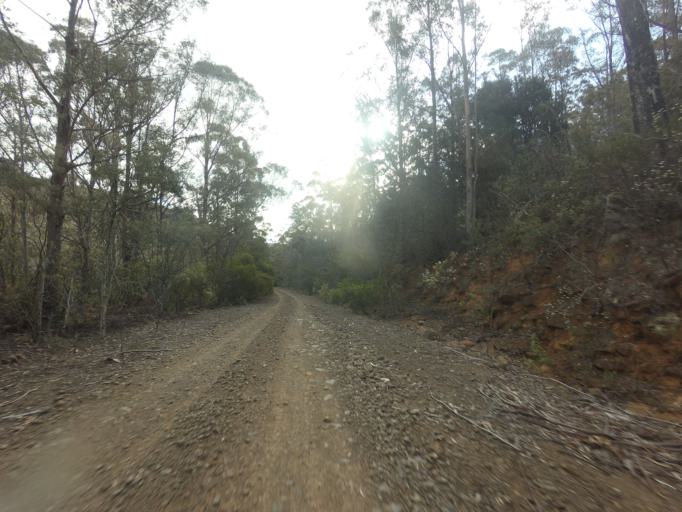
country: AU
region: Tasmania
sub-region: Break O'Day
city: St Helens
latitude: -41.8535
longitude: 148.0416
